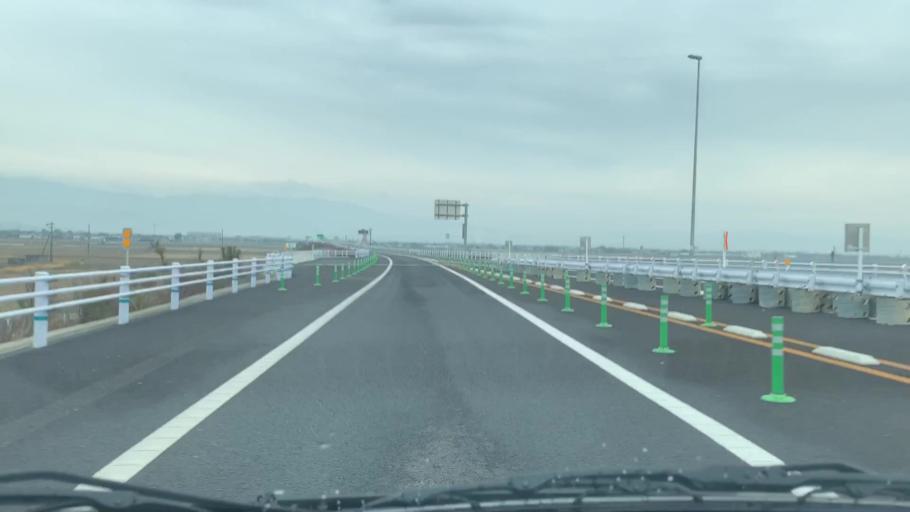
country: JP
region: Saga Prefecture
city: Saga-shi
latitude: 33.2054
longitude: 130.2151
